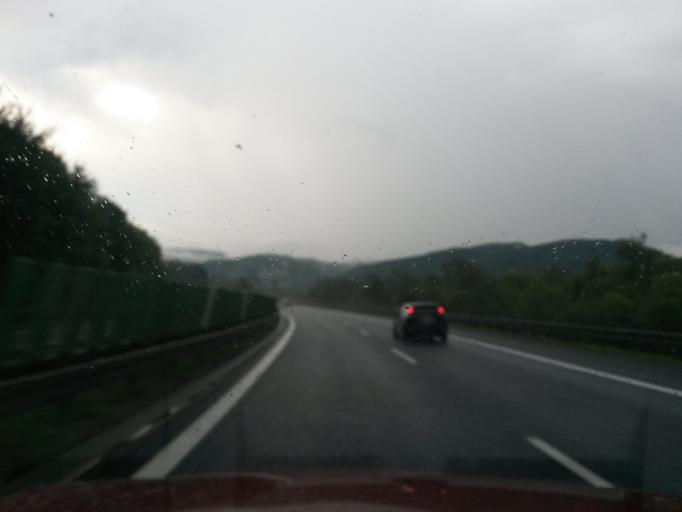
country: PL
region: Lesser Poland Voivodeship
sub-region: Powiat myslenicki
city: Pcim
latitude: 49.7395
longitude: 19.9773
